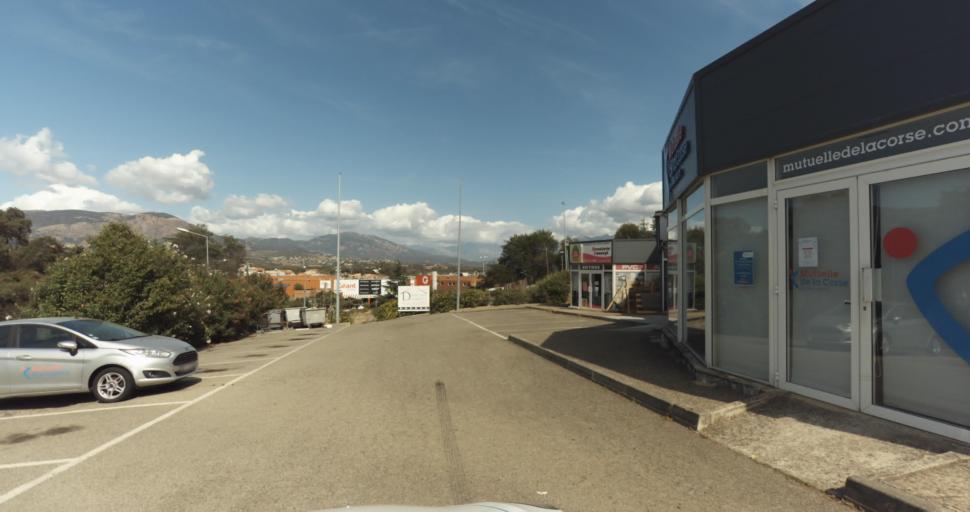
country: FR
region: Corsica
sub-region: Departement de la Corse-du-Sud
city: Afa
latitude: 41.9481
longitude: 8.7743
